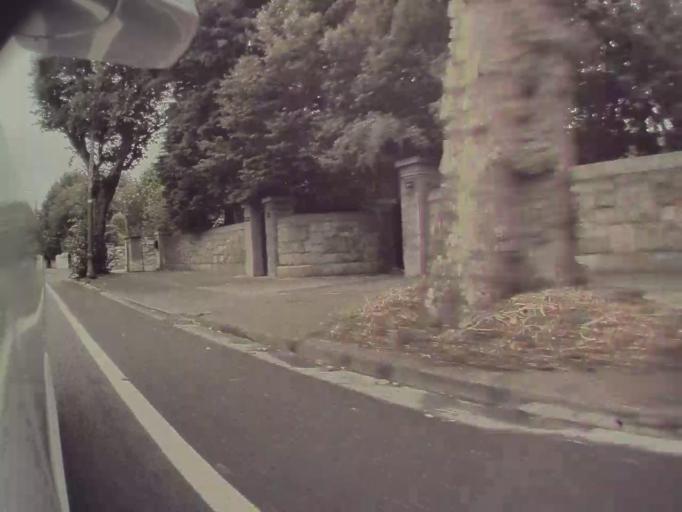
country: IE
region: Leinster
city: Donnybrook
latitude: 53.3229
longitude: -6.2189
